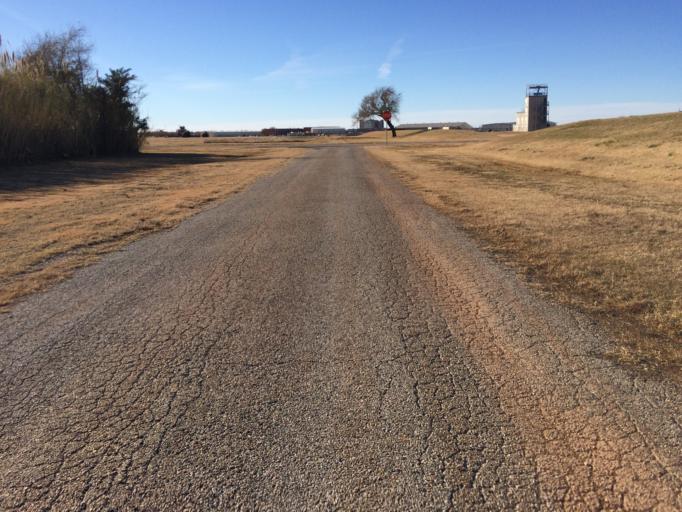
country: US
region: Oklahoma
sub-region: Cleveland County
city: Norman
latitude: 35.2428
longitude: -97.4593
